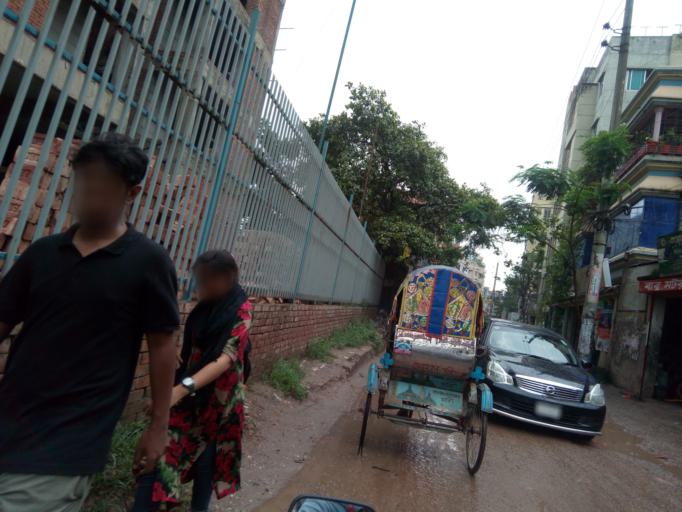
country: BD
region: Dhaka
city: Azimpur
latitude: 23.7584
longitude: 90.3597
